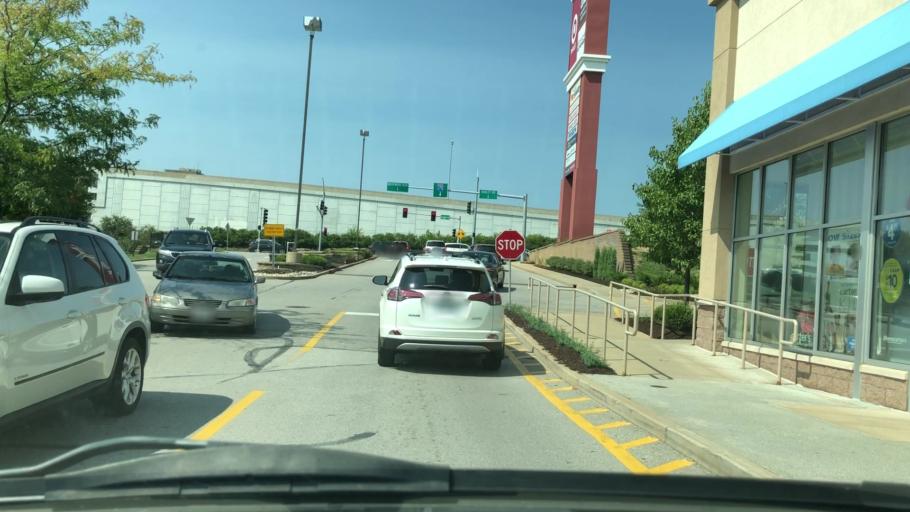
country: US
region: Missouri
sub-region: Saint Louis County
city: Brentwood
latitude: 38.6280
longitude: -90.3416
